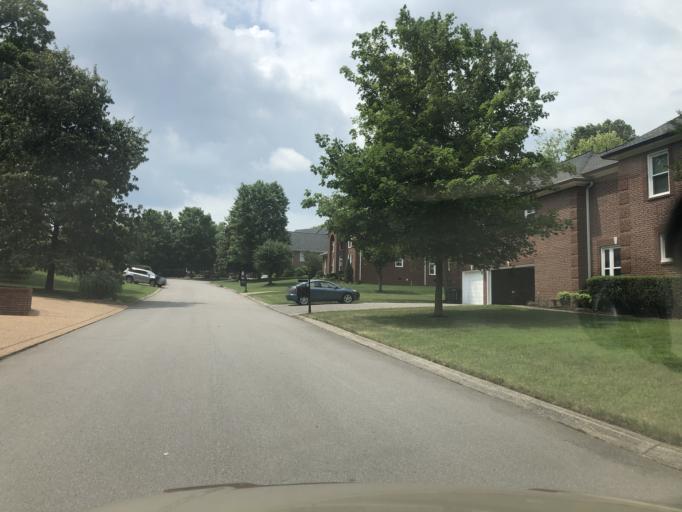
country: US
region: Tennessee
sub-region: Davidson County
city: Lakewood
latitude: 36.2353
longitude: -86.6041
